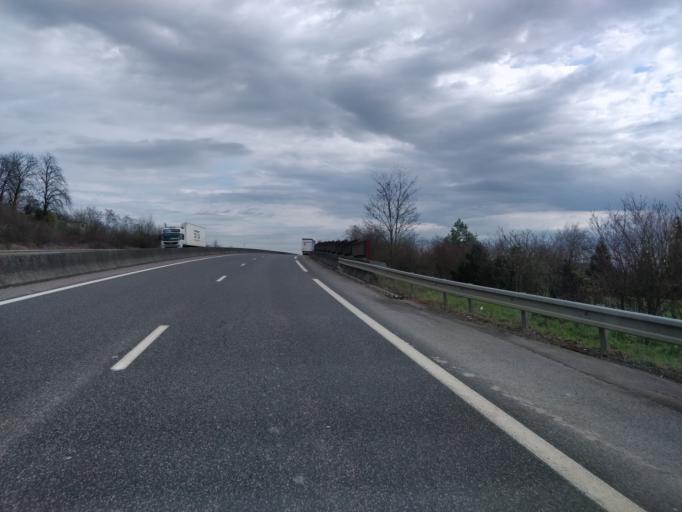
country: FR
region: Lorraine
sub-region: Departement de la Moselle
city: Gandrange
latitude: 49.2738
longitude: 6.1143
